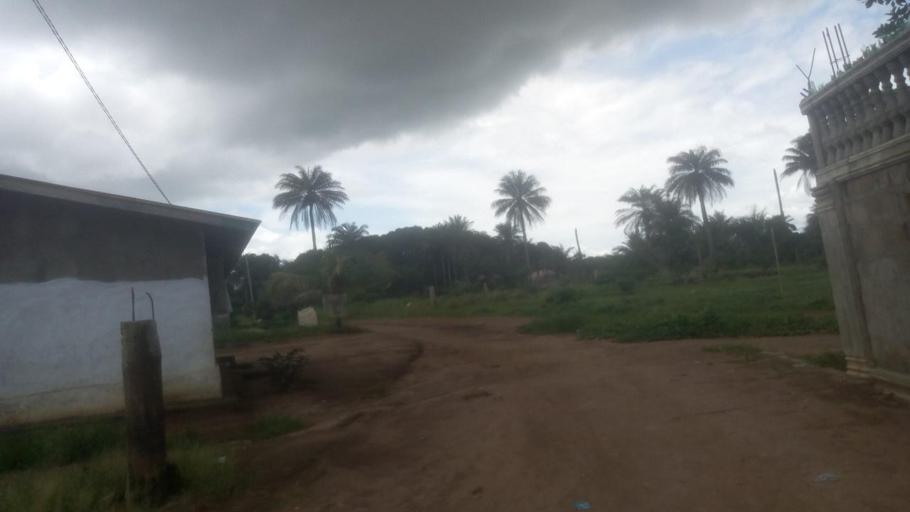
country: SL
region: Northern Province
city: Masoyila
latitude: 8.5849
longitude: -13.1665
